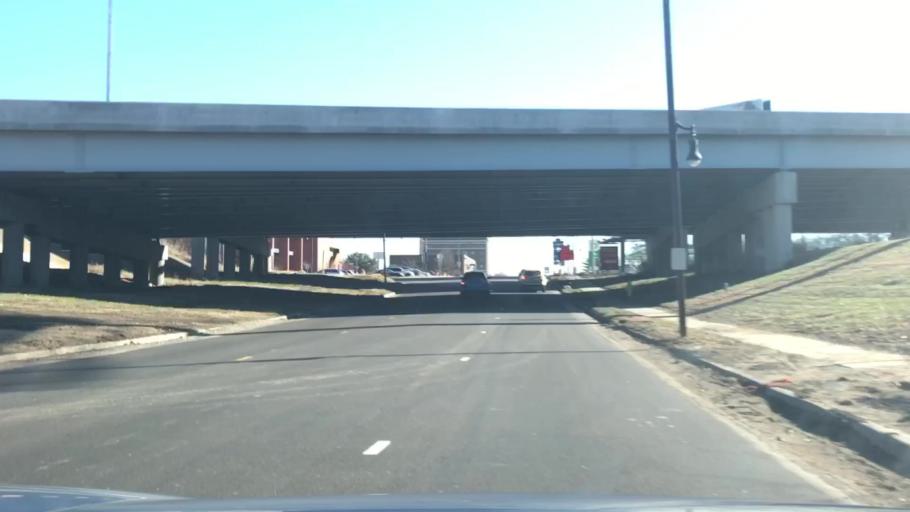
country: US
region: Illinois
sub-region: Saint Clair County
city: East Saint Louis
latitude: 38.6272
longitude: -90.1644
